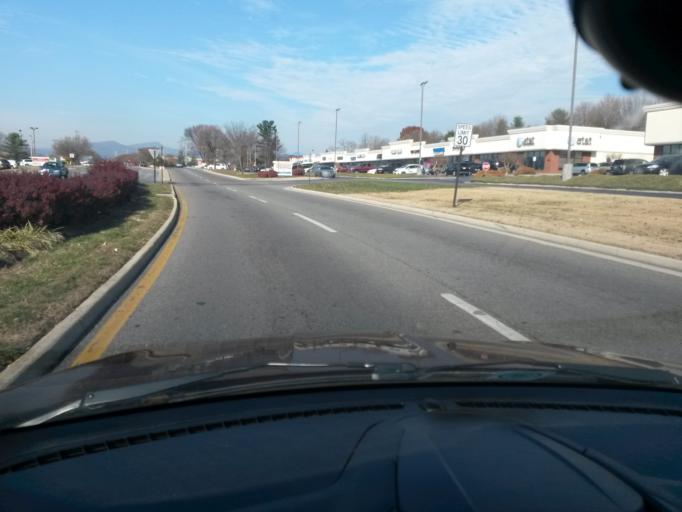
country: US
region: Virginia
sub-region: City of Roanoke
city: Roanoke
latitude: 37.3008
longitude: -79.9563
